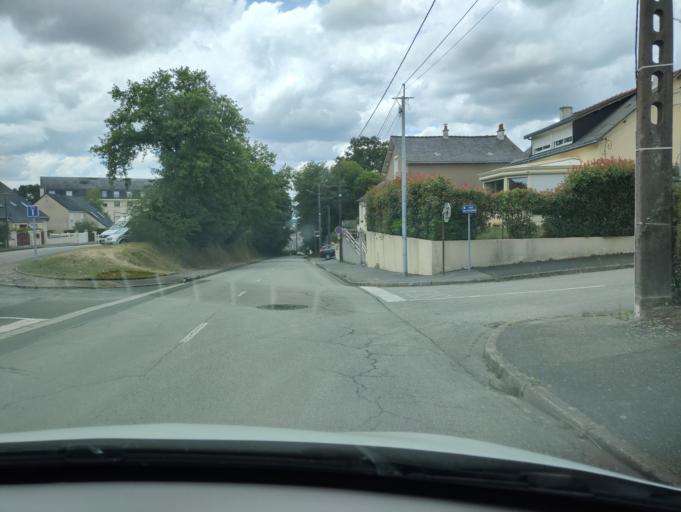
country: FR
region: Pays de la Loire
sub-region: Departement de la Loire-Atlantique
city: Chateaubriant
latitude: 47.7163
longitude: -1.3661
